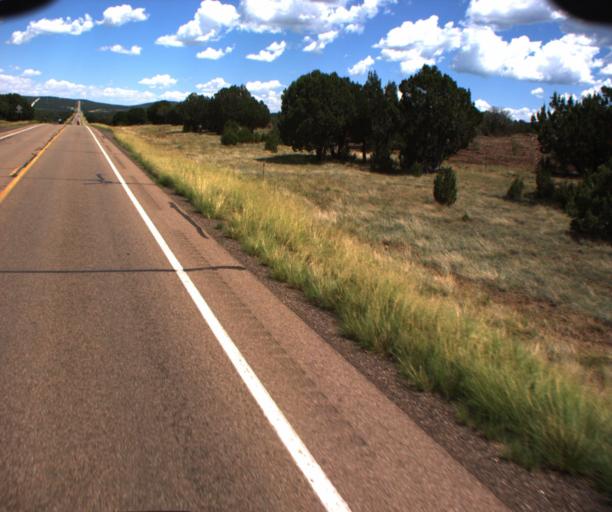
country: US
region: Arizona
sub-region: Navajo County
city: White Mountain Lake
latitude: 34.2793
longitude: -109.8751
